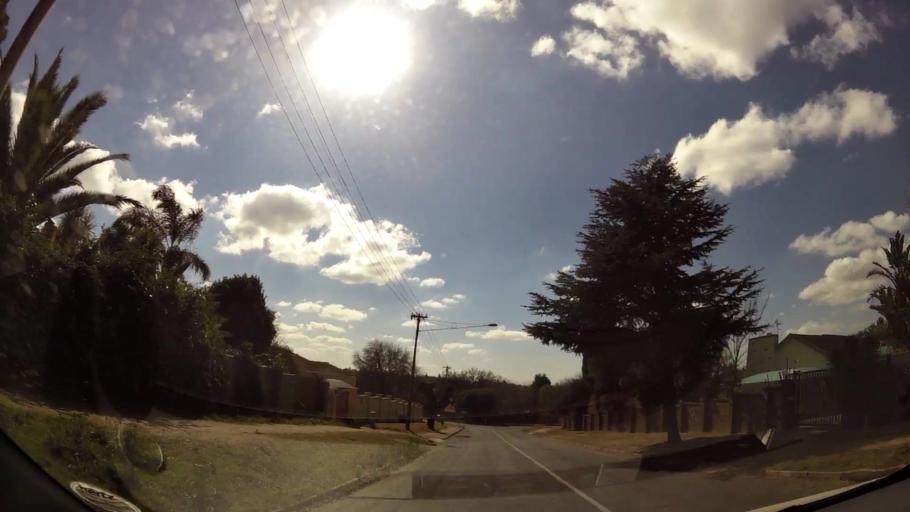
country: ZA
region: Gauteng
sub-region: West Rand District Municipality
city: Krugersdorp
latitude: -26.1192
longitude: 27.8216
